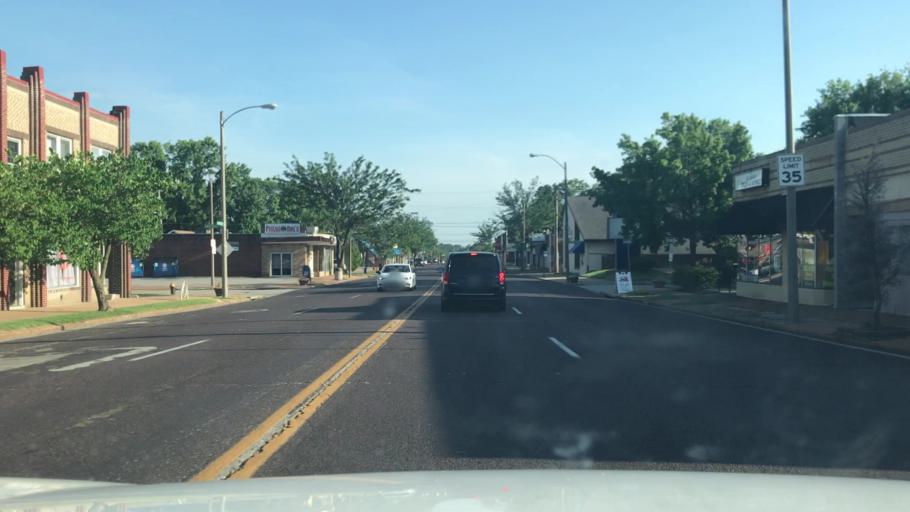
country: US
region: Missouri
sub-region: Saint Louis County
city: Maplewood
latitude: 38.5864
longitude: -90.2927
